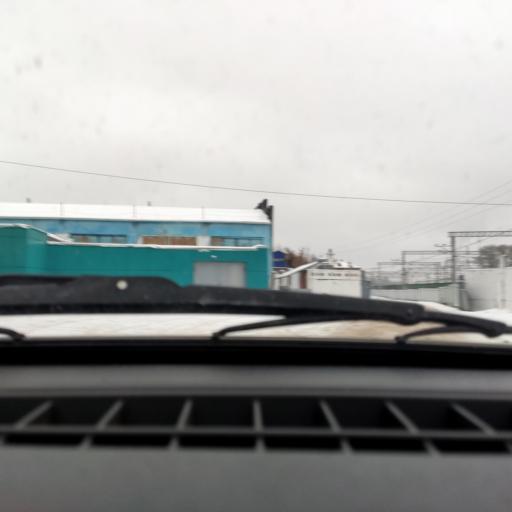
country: RU
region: Bashkortostan
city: Ufa
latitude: 54.8063
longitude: 56.1004
